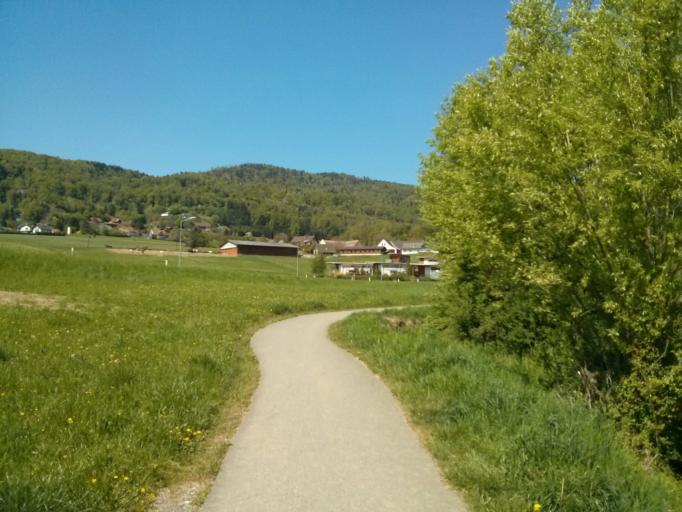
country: AT
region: Styria
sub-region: Politischer Bezirk Graz-Umgebung
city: Stattegg
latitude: 47.1397
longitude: 15.4193
